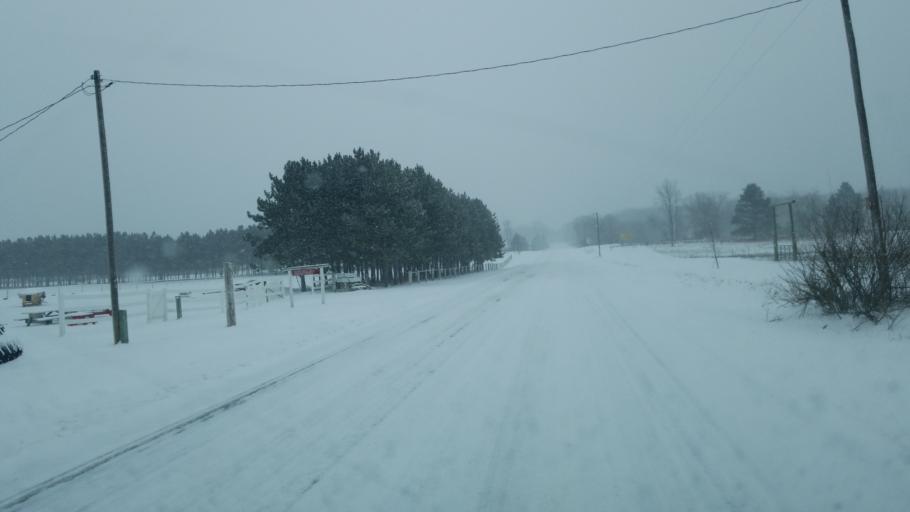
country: US
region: Michigan
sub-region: Mecosta County
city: Canadian Lakes
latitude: 43.5905
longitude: -85.3365
